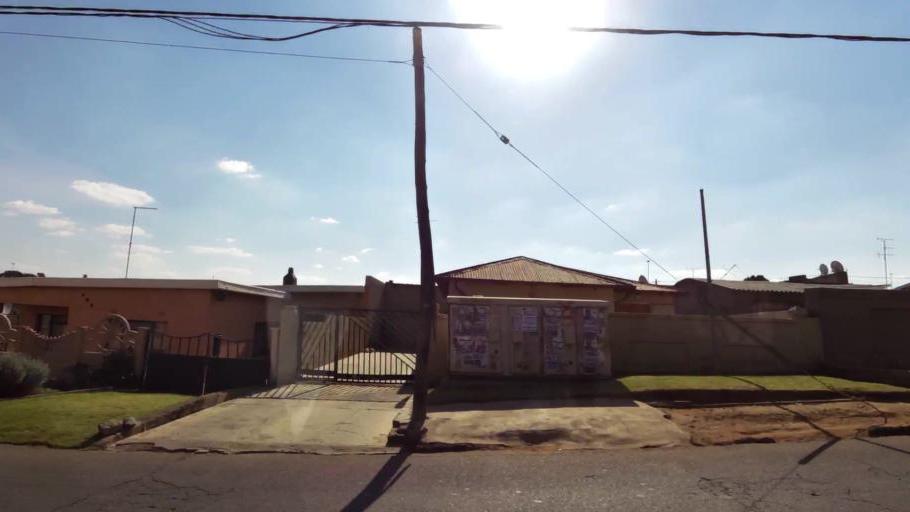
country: ZA
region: Gauteng
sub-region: City of Johannesburg Metropolitan Municipality
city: Soweto
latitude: -26.2344
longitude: 27.8902
